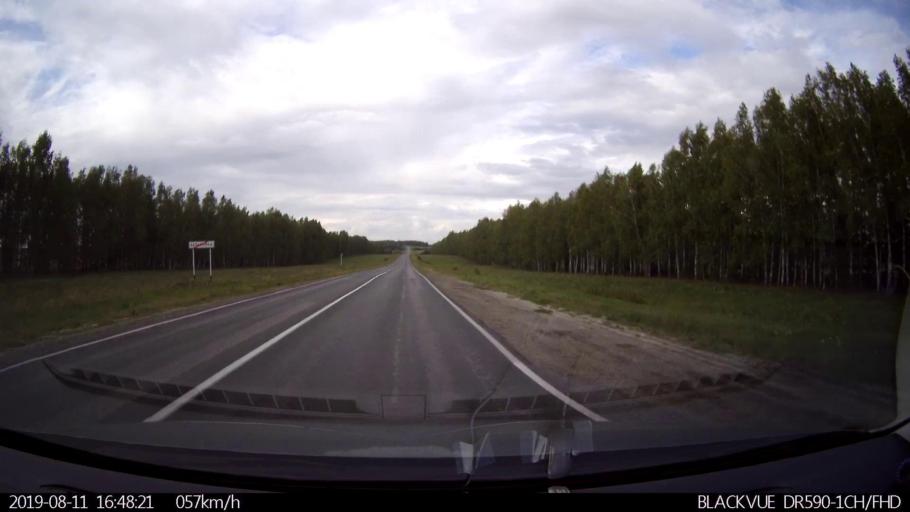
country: RU
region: Ulyanovsk
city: Mayna
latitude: 54.2082
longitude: 47.6920
